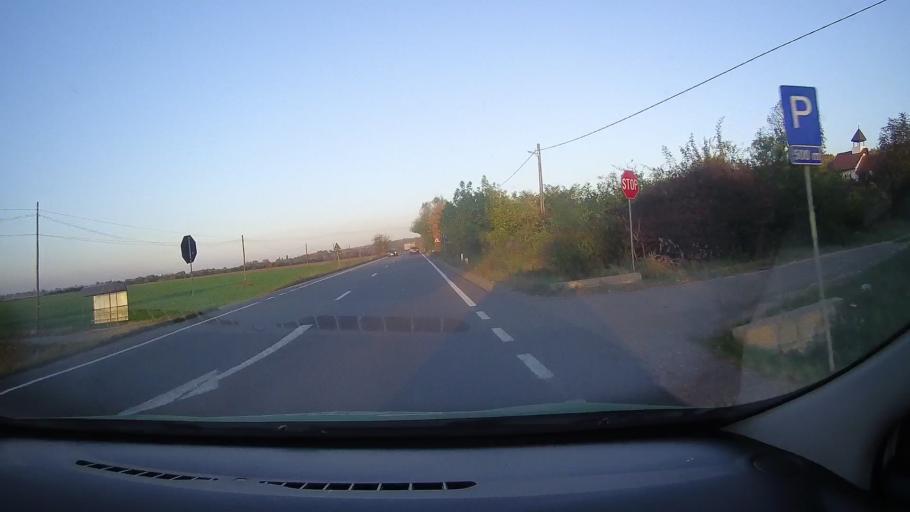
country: RO
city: Dioszeg
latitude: 47.2877
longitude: 21.9978
